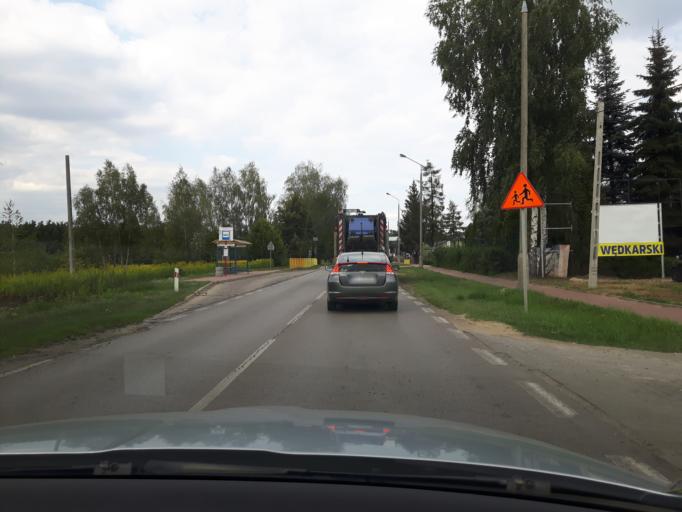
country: PL
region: Masovian Voivodeship
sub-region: Powiat legionowski
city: Stanislawow Pierwszy
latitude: 52.3932
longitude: 21.0335
